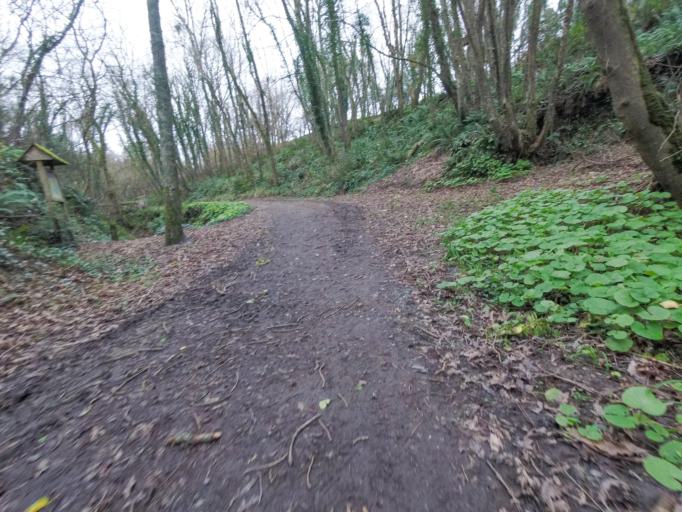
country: IE
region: Munster
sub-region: Waterford
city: Tra Mhor
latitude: 52.1436
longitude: -7.1687
